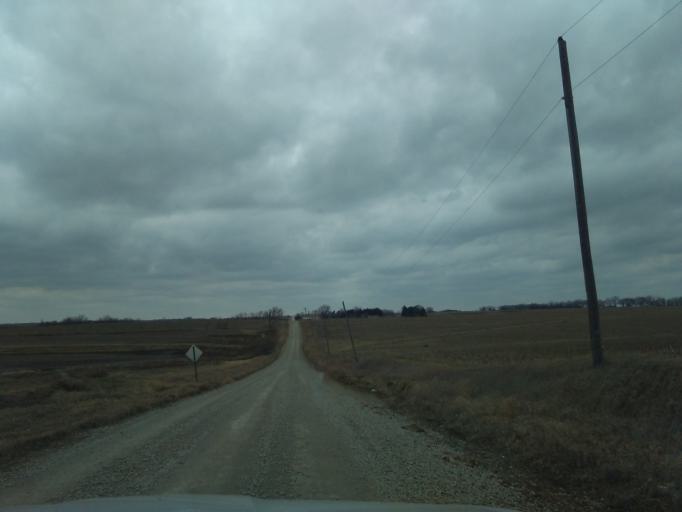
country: US
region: Nebraska
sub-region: Pawnee County
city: Pawnee City
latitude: 40.0587
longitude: -96.0495
